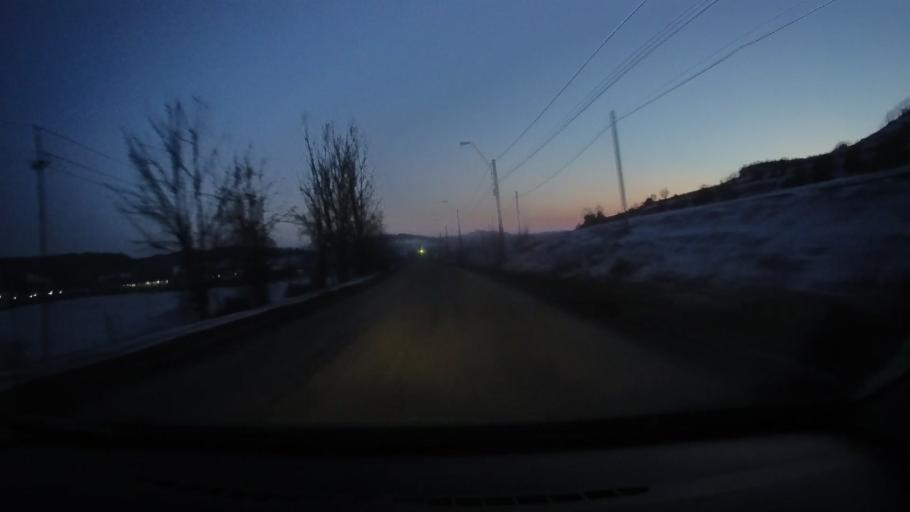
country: RO
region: Sibiu
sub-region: Municipiul Medias
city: Medias
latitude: 46.1818
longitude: 24.3697
